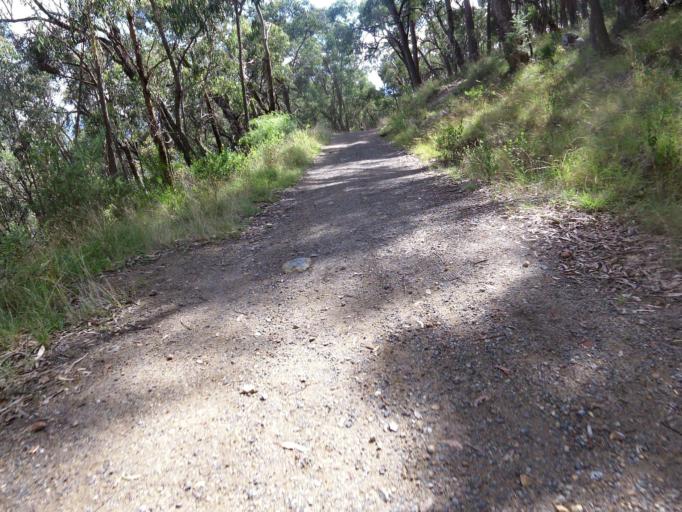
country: AU
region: Victoria
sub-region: Knox
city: The Basin
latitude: -37.8373
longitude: 145.3356
